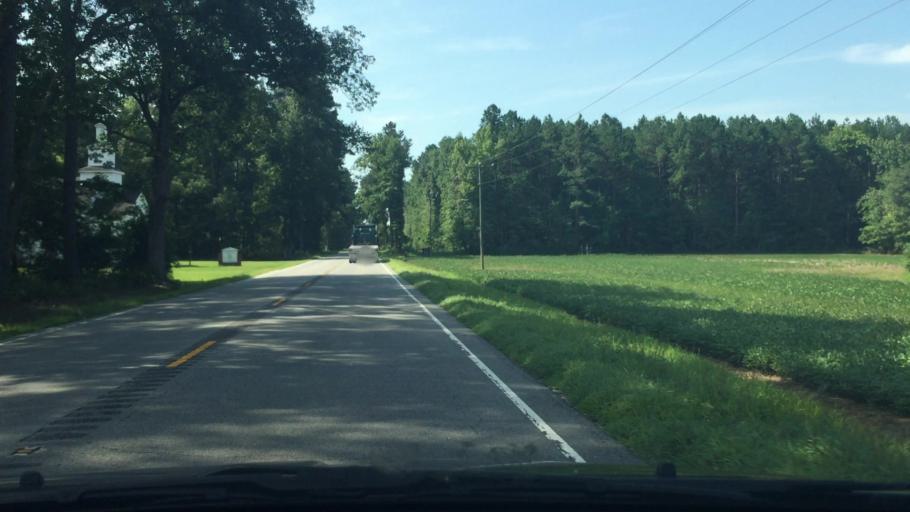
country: US
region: Virginia
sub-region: Sussex County
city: Sussex
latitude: 36.8953
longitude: -77.1525
